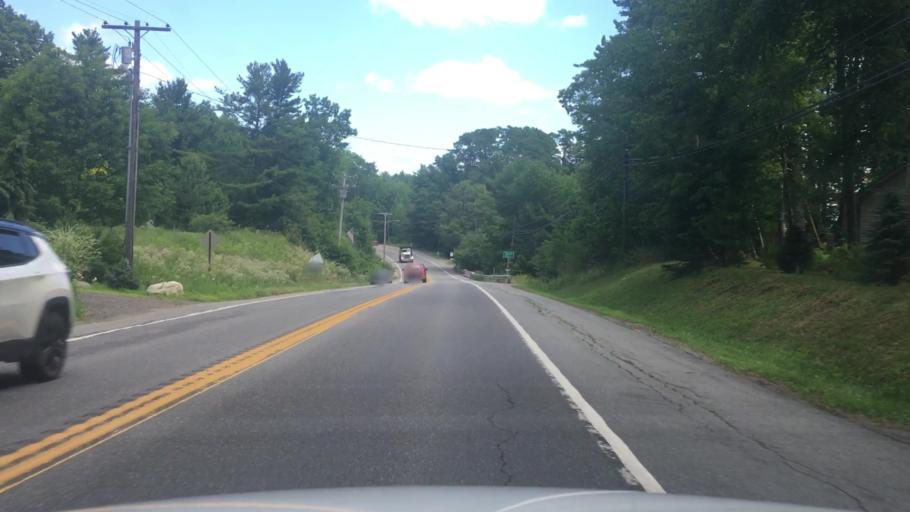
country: US
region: Maine
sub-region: Waldo County
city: Belfast
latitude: 44.3934
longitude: -68.9896
